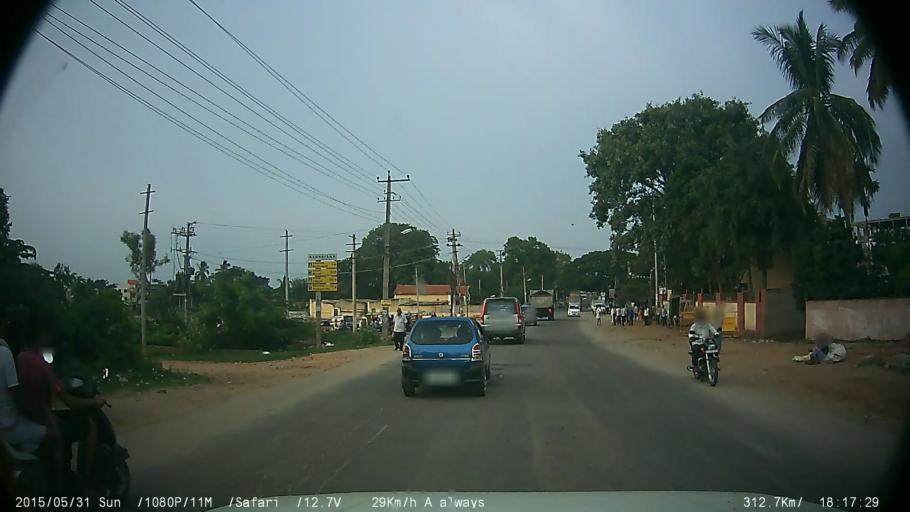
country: IN
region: Karnataka
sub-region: Mysore
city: Nanjangud
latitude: 12.1191
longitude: 76.6751
